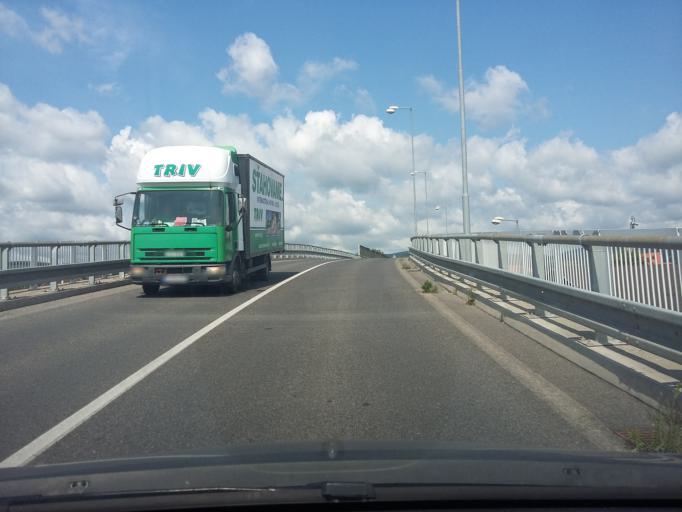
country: SK
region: Bratislavsky
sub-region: Okres Pezinok
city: Pezinok
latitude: 48.2672
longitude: 17.2475
